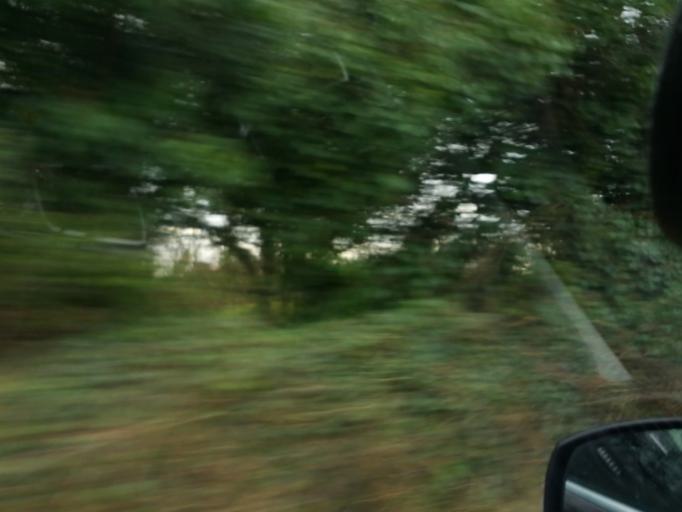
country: IE
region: Connaught
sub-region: County Galway
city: Athenry
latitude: 53.2309
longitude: -8.7733
